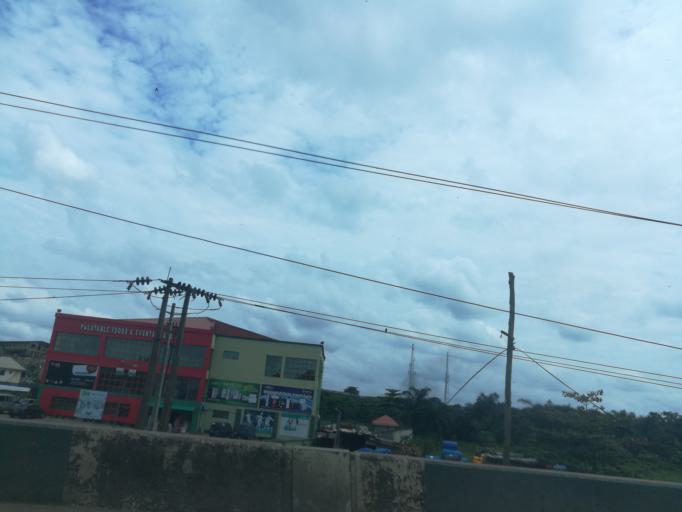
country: NG
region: Lagos
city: Ikotun
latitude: 6.4998
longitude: 3.1013
